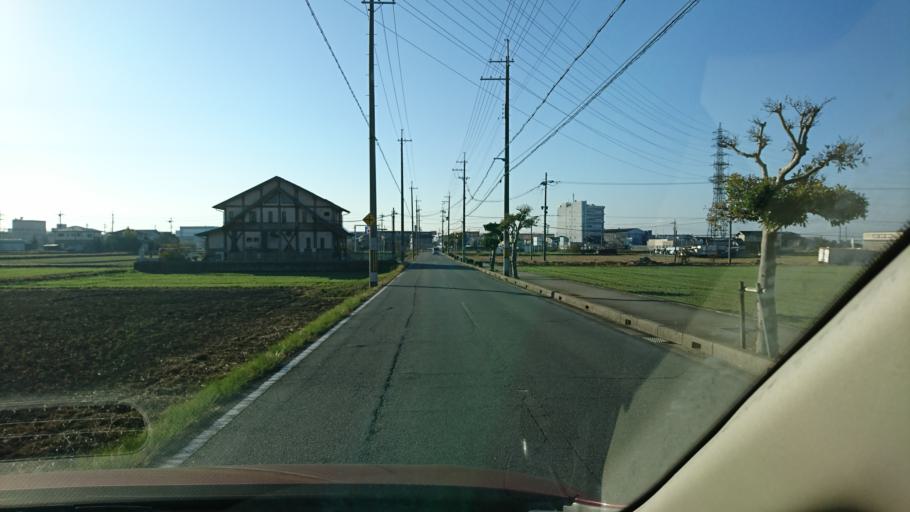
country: JP
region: Hyogo
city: Miki
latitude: 34.7359
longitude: 134.9223
